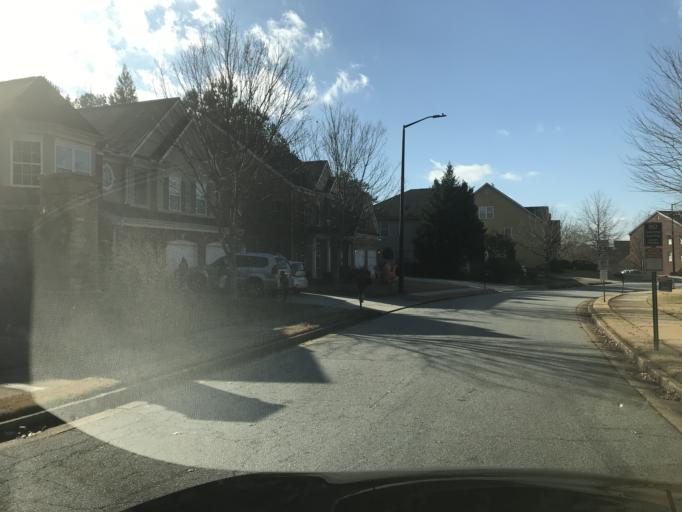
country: US
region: Georgia
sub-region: Cobb County
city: Mableton
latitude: 33.7146
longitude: -84.5595
